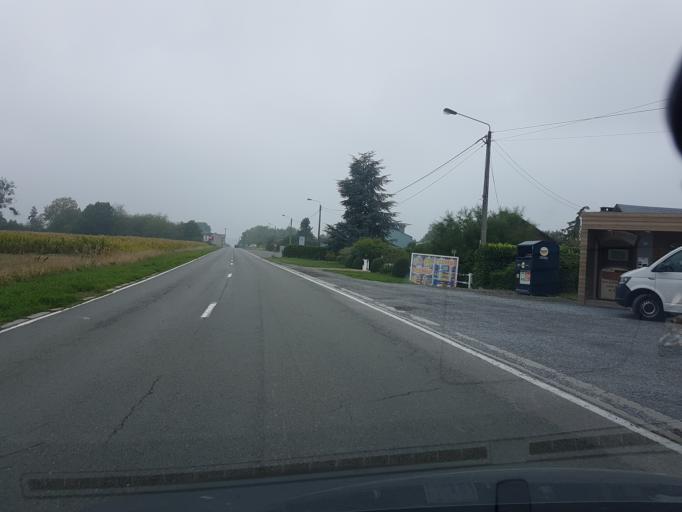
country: BE
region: Wallonia
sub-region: Province de Namur
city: Ohey
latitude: 50.4528
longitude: 5.1146
